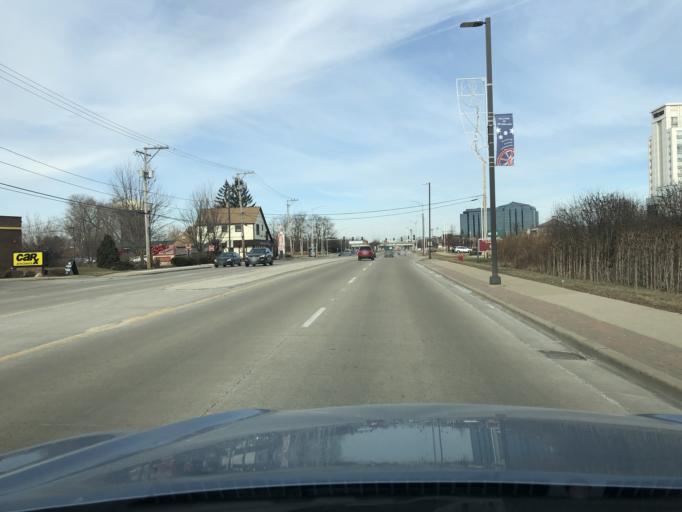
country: US
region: Illinois
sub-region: Cook County
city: Wheeling
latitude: 42.1484
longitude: -87.9120
